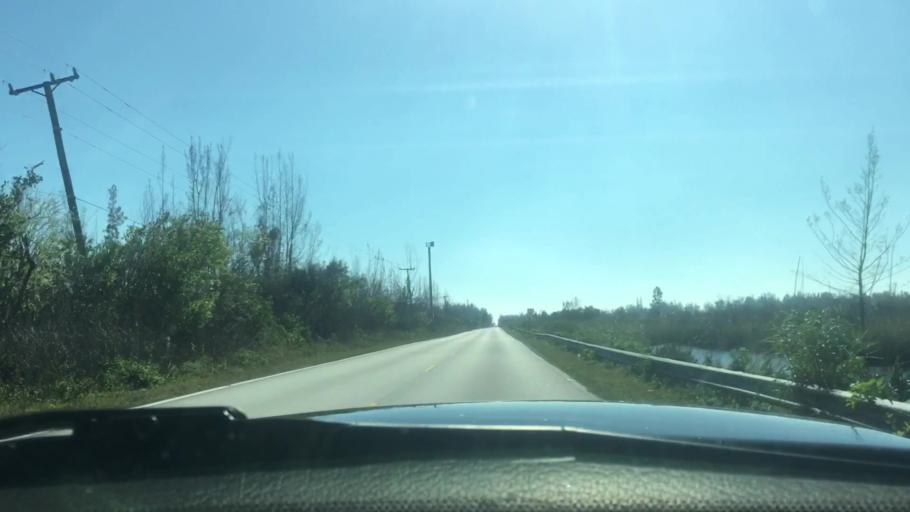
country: US
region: Florida
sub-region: Miami-Dade County
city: Florida City
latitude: 25.4277
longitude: -80.4695
